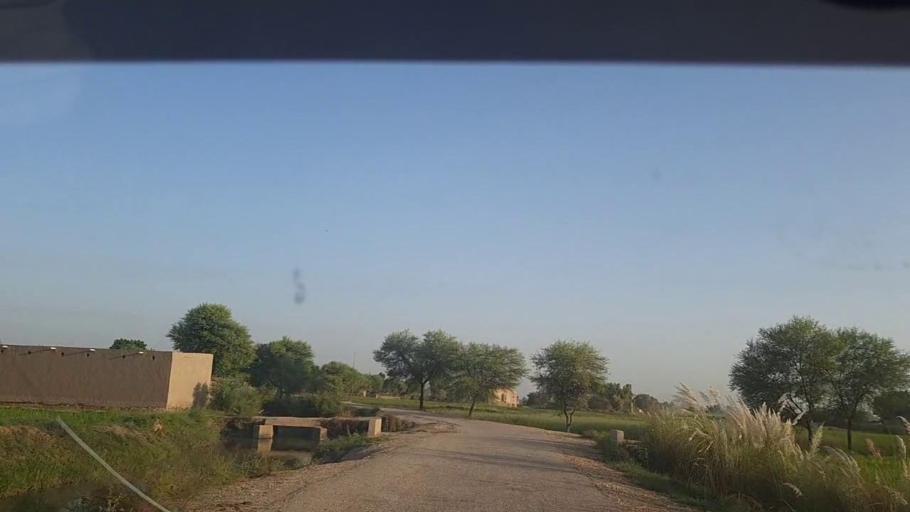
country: PK
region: Sindh
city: Thul
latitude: 28.1209
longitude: 68.8954
